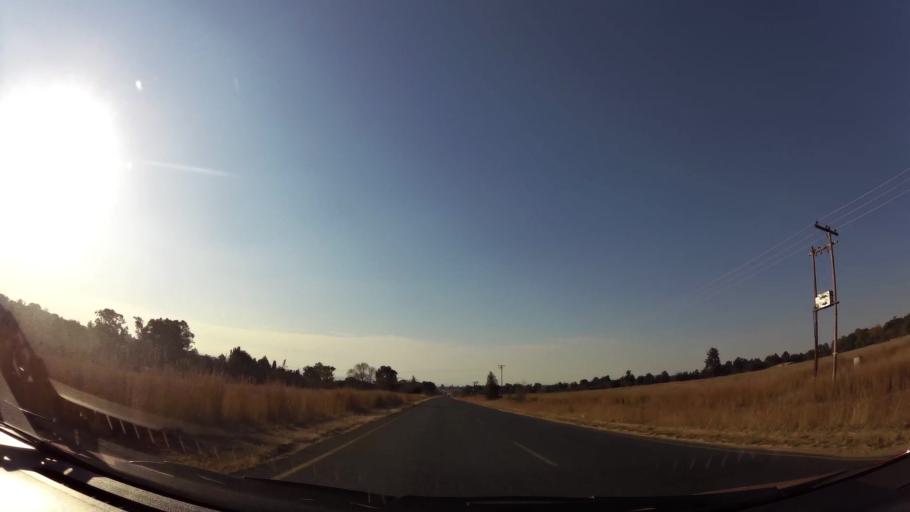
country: ZA
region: Gauteng
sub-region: West Rand District Municipality
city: Muldersdriseloop
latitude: -26.0221
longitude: 27.9087
